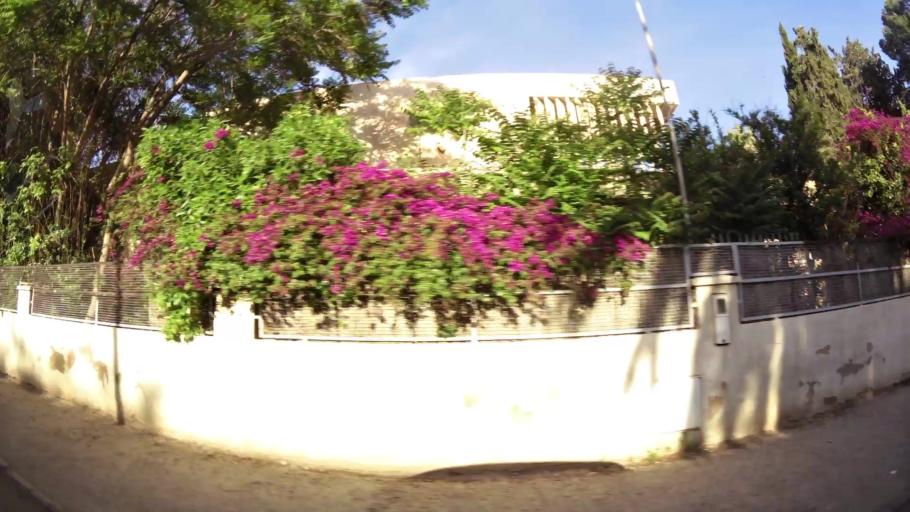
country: MA
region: Oriental
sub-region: Oujda-Angad
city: Oujda
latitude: 34.6760
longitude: -1.9133
